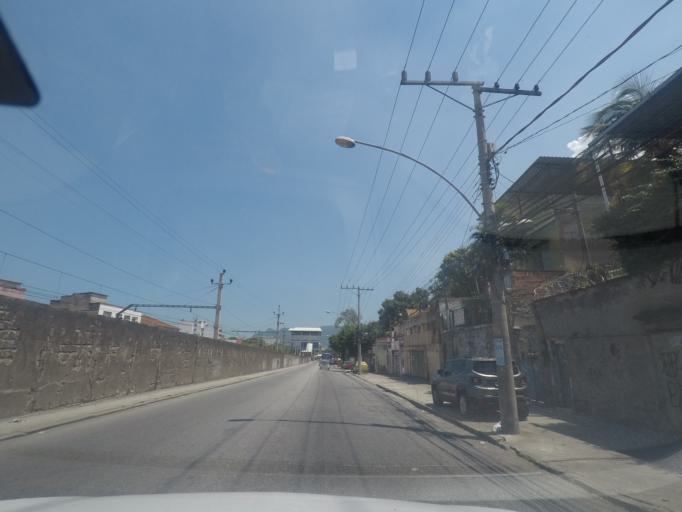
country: BR
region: Rio de Janeiro
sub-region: Rio De Janeiro
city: Rio de Janeiro
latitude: -22.8643
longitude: -43.2566
